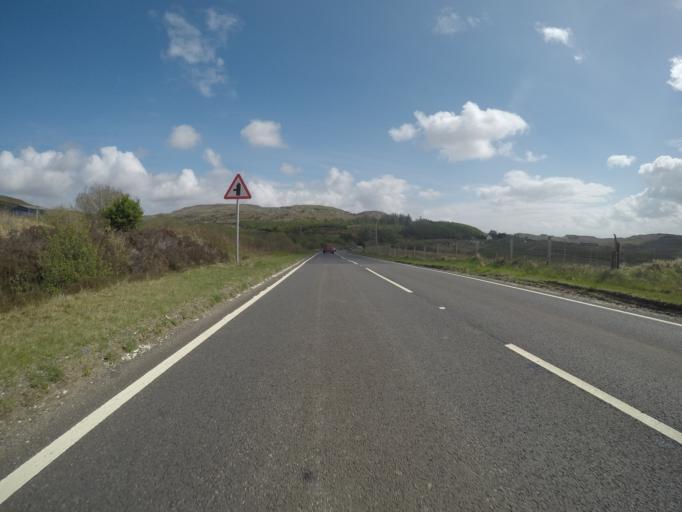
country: GB
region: Scotland
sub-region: Highland
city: Portree
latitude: 57.5321
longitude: -6.3535
